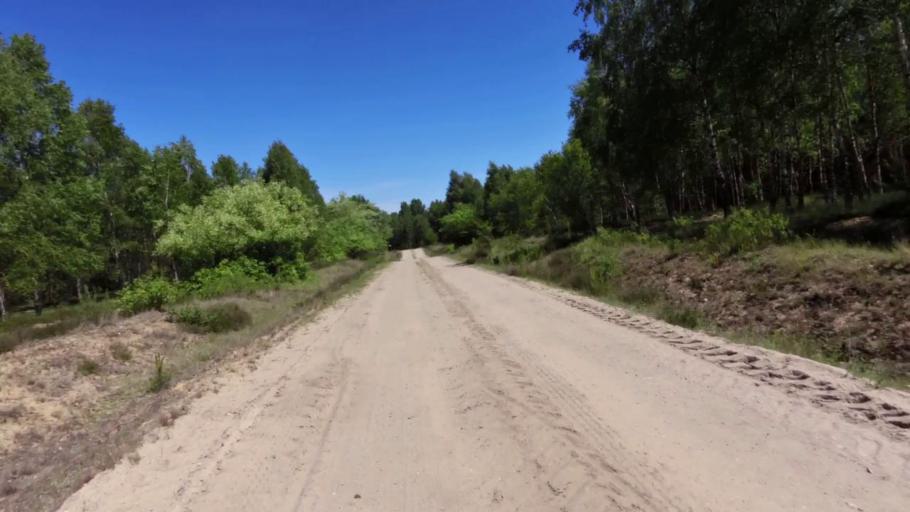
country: PL
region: West Pomeranian Voivodeship
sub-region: Powiat szczecinecki
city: Borne Sulinowo
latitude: 53.5855
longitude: 16.6523
